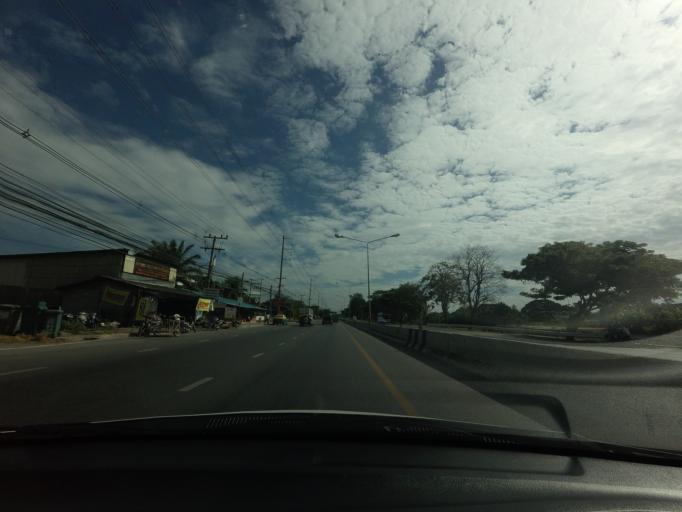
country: TH
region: Pathum Thani
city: Ban Rangsit
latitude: 14.0513
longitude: 100.8200
